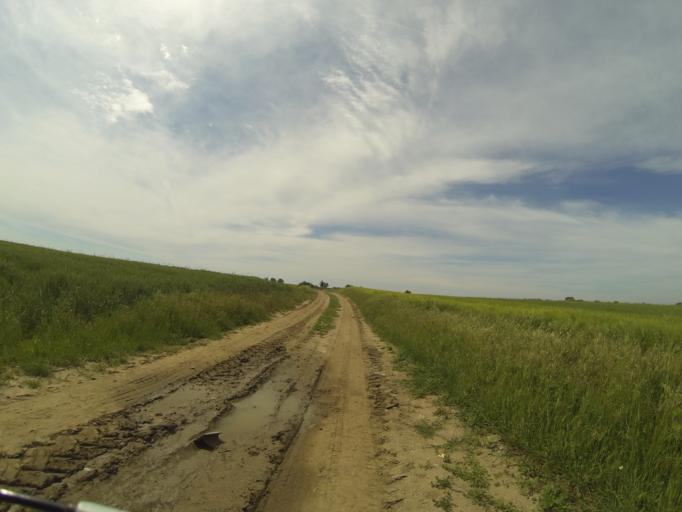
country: RO
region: Dolj
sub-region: Comuna Ghindeni
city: Ghindeni
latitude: 44.2093
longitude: 23.9386
